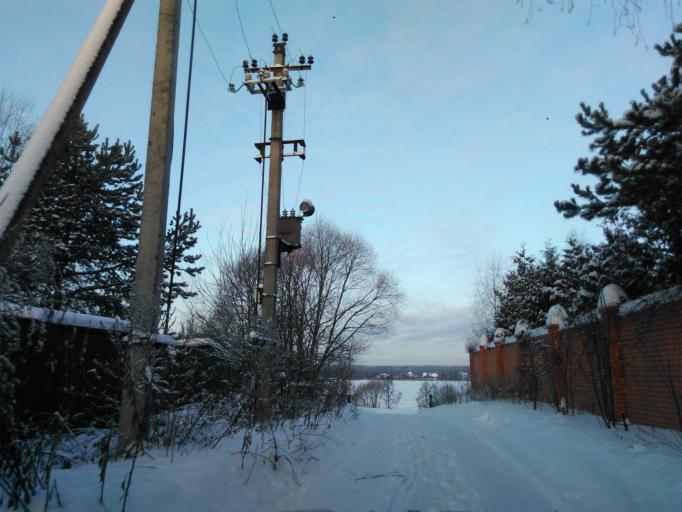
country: RU
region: Tverskaya
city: Zavidovo
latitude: 56.6369
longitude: 36.6175
